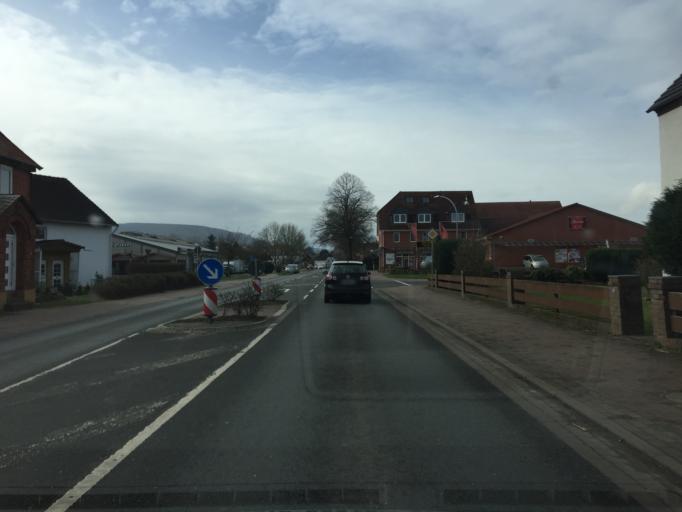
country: DE
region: Lower Saxony
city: Aerzen
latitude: 52.0692
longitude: 9.3078
